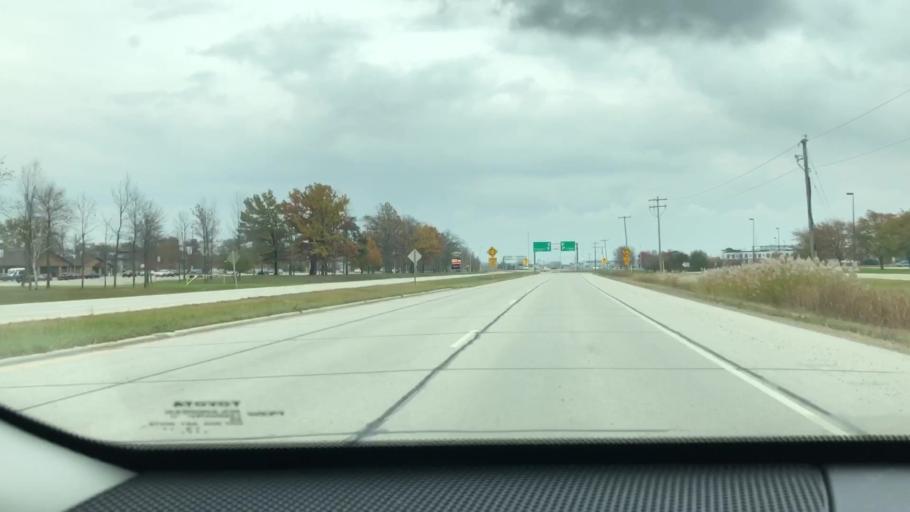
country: US
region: Wisconsin
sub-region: Brown County
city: Oneida
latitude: 44.4956
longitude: -88.1289
